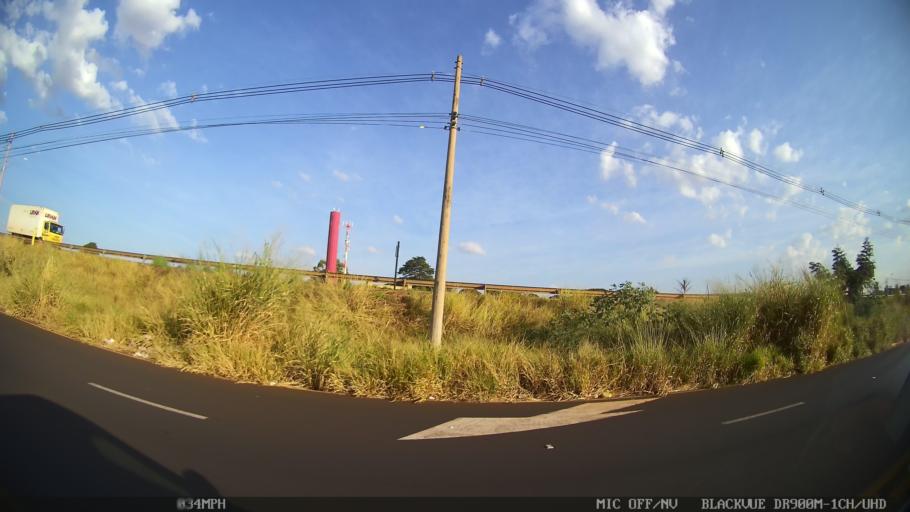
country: BR
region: Sao Paulo
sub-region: Ribeirao Preto
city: Ribeirao Preto
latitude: -21.2058
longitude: -47.7519
